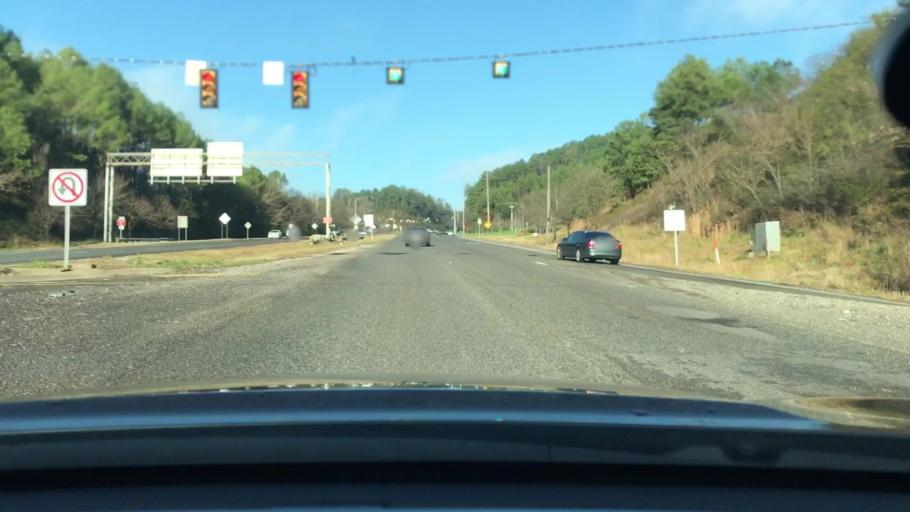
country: US
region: Alabama
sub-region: Jefferson County
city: Cahaba Heights
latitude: 33.4429
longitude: -86.7312
